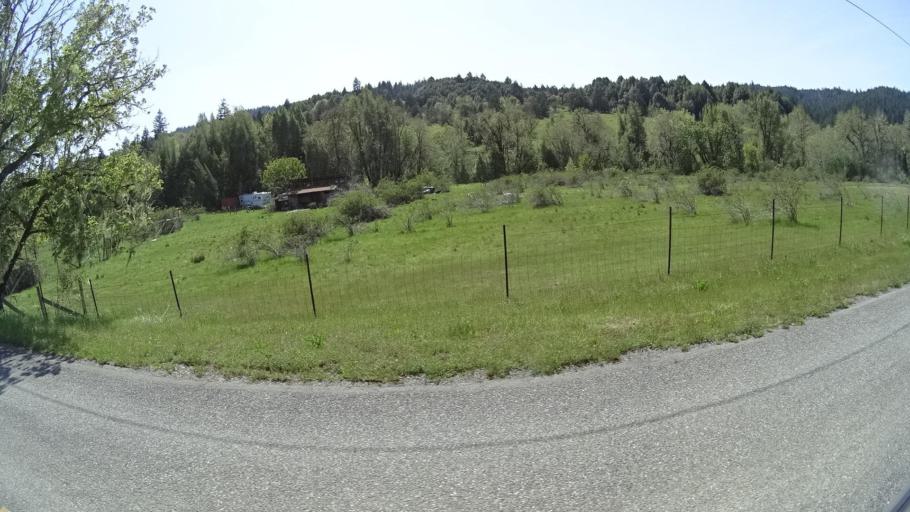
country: US
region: California
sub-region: Humboldt County
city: Redway
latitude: 40.2965
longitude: -123.6509
